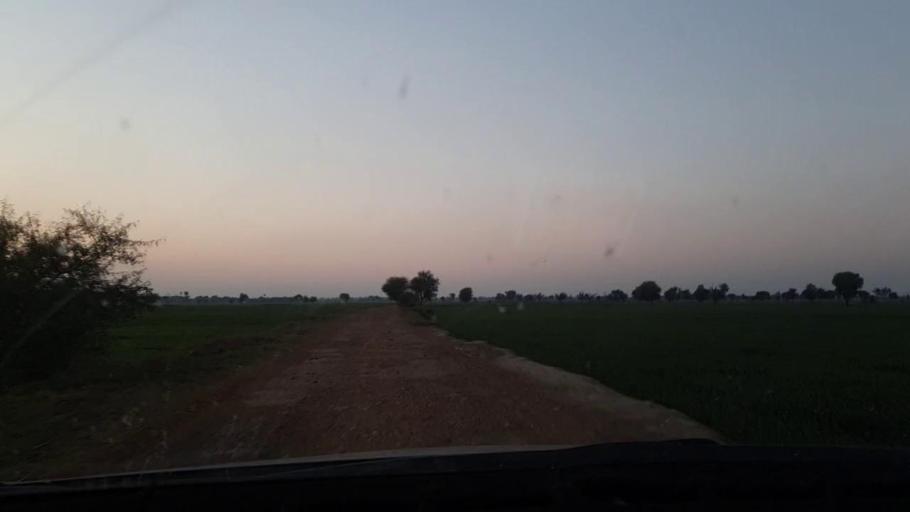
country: PK
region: Sindh
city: Tando Mittha Khan
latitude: 25.9313
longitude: 69.3258
